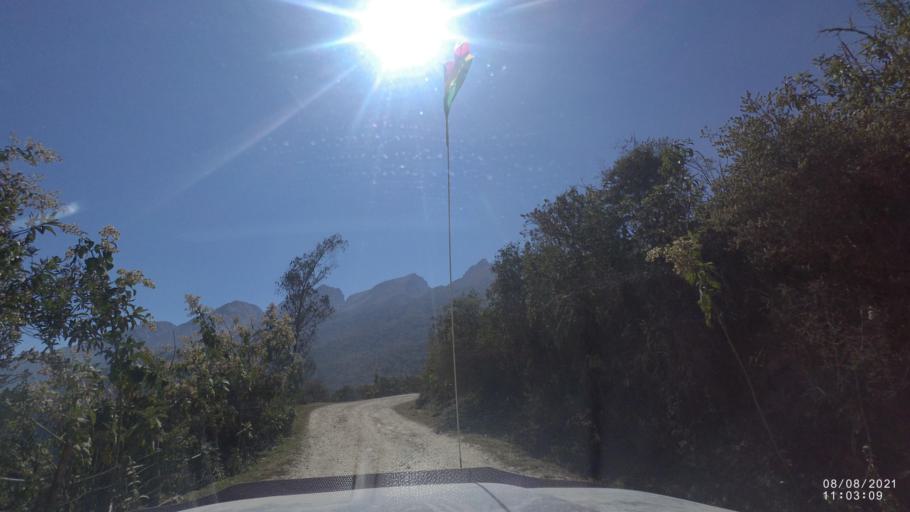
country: BO
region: Cochabamba
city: Colchani
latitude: -16.7545
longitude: -66.6873
